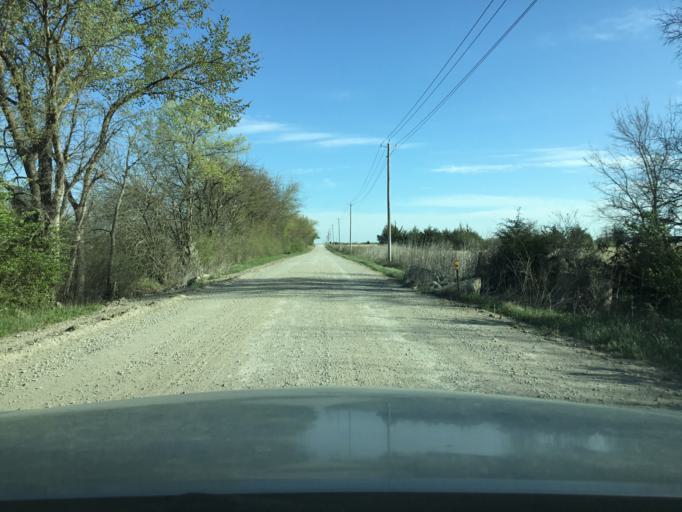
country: US
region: Kansas
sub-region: Neosho County
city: Chanute
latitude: 37.6551
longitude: -95.4893
